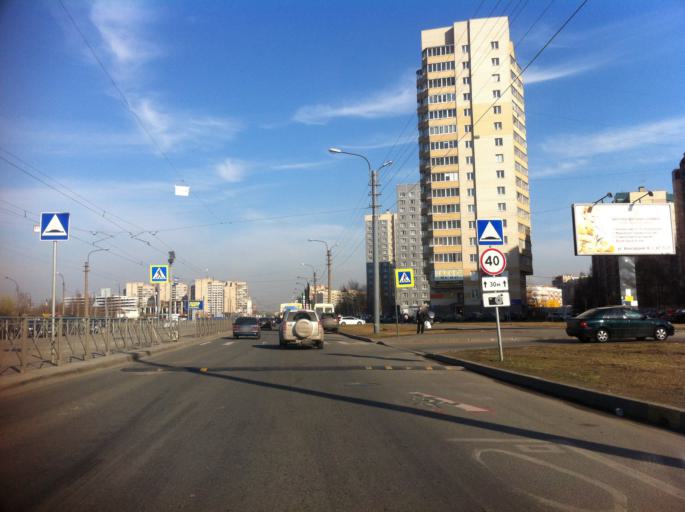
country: RU
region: St.-Petersburg
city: Dachnoye
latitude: 59.8598
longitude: 30.2209
